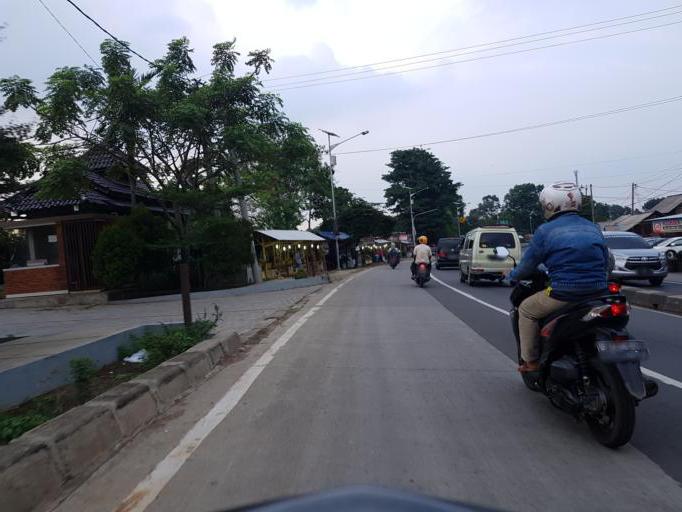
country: ID
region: West Java
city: Parung
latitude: -6.4888
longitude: 106.7363
